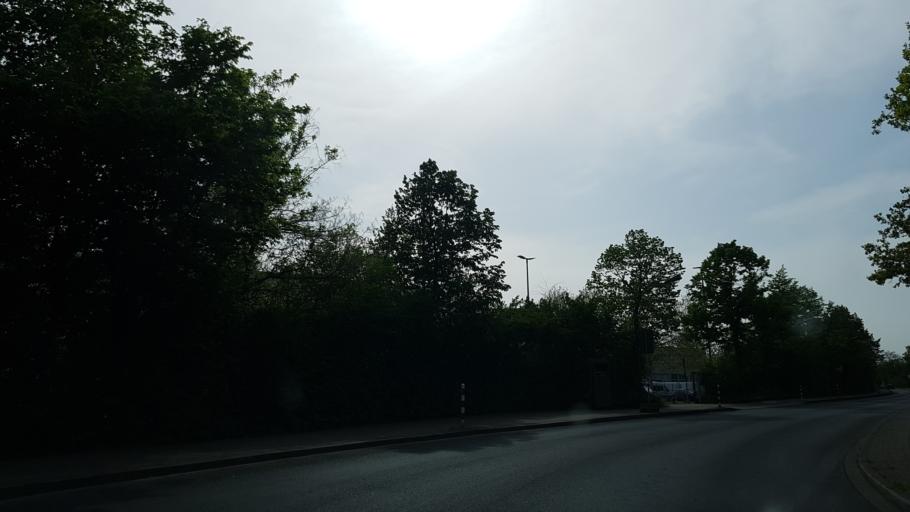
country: DE
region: North Rhine-Westphalia
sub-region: Regierungsbezirk Dusseldorf
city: Dusseldorf
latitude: 51.2632
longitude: 6.7884
